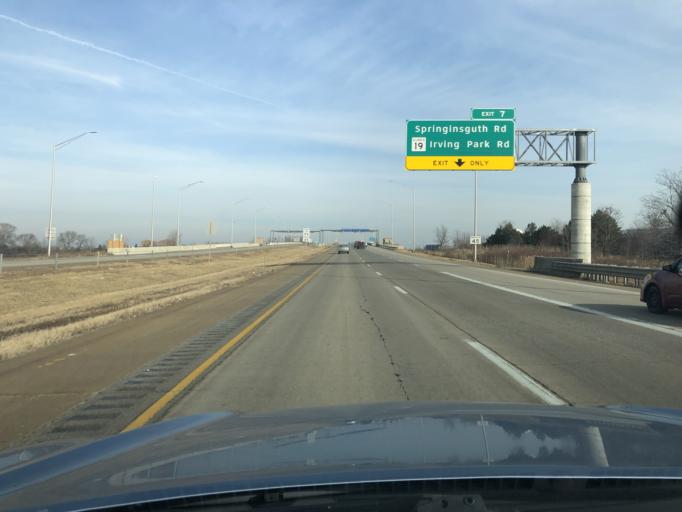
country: US
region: Illinois
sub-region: DuPage County
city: Hanover Park
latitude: 41.9853
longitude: -88.1322
